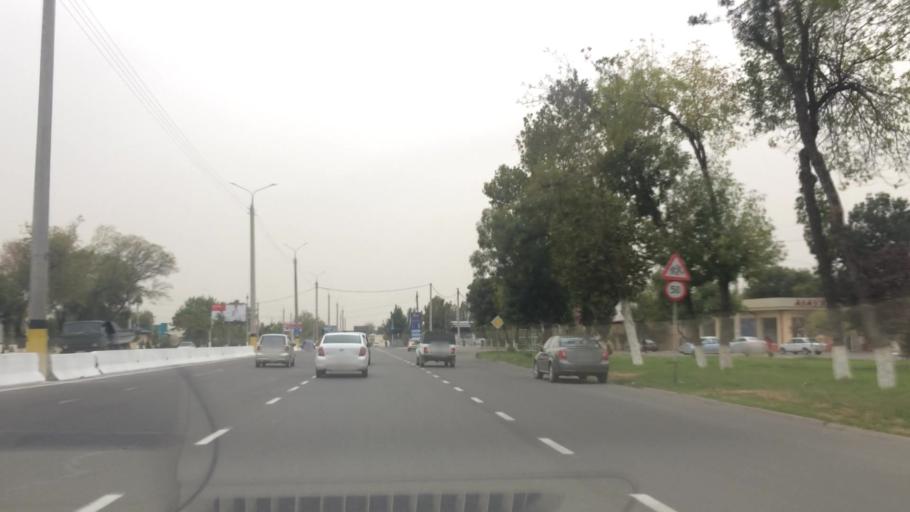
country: UZ
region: Toshkent
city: Salor
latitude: 41.3118
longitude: 69.3472
